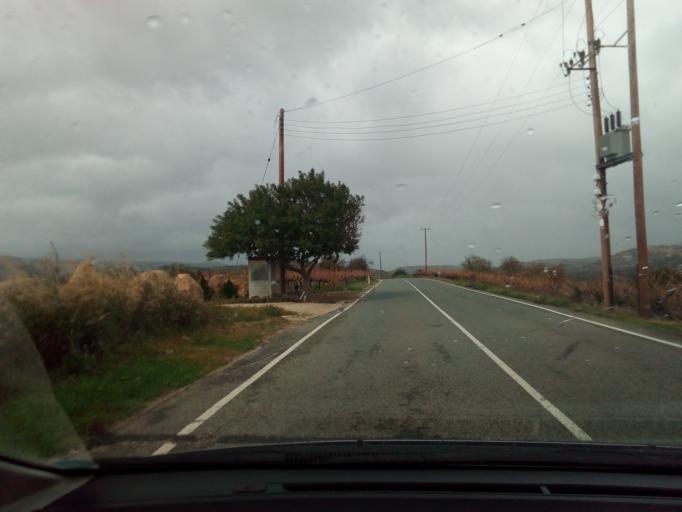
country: CY
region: Pafos
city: Polis
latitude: 34.9549
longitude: 32.4821
